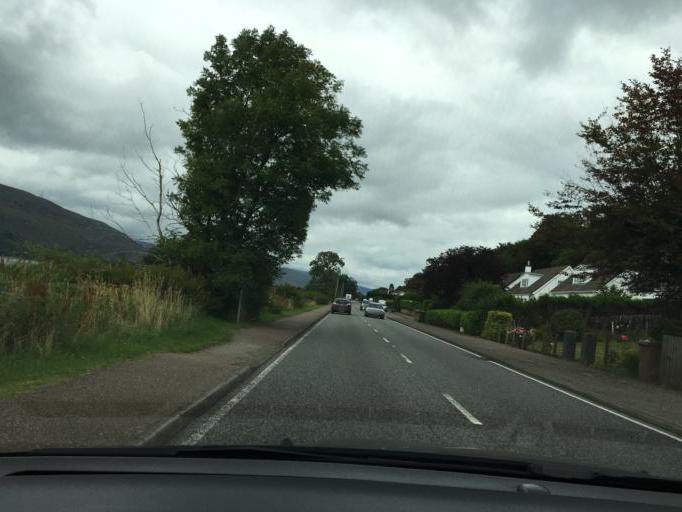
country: GB
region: Scotland
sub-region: Highland
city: Fort William
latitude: 56.7990
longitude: -5.1375
